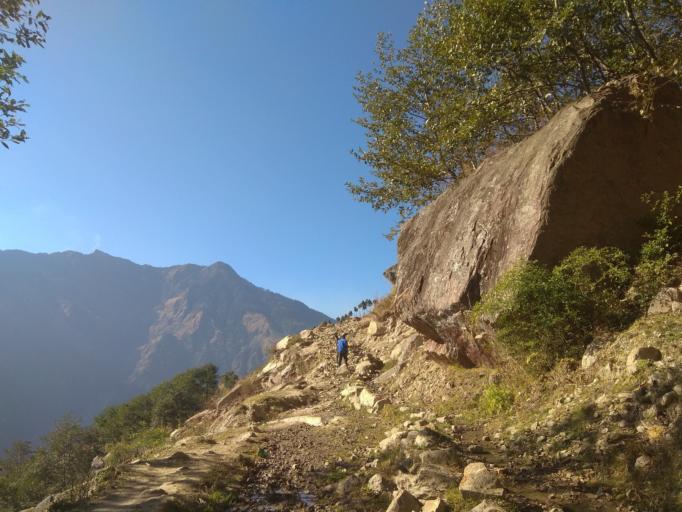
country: NP
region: Far Western
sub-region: Seti Zone
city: Achham
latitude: 29.2584
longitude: 81.6334
